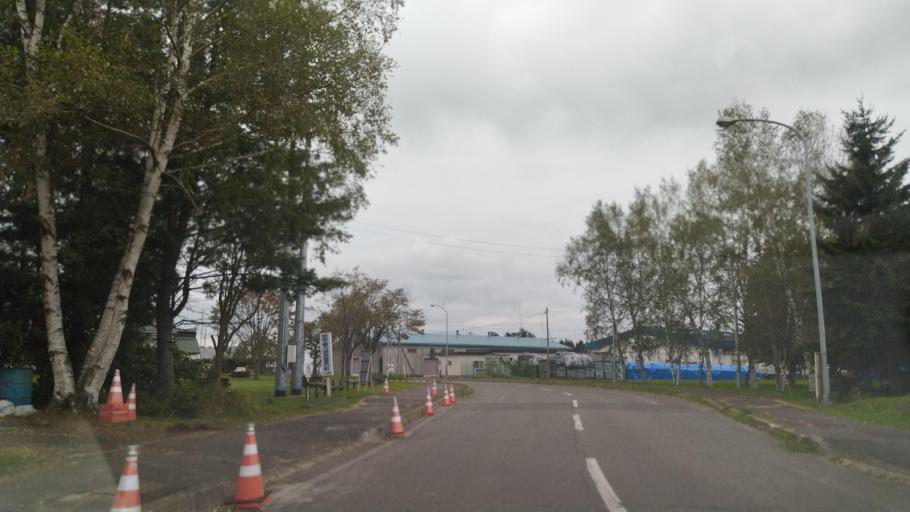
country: JP
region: Hokkaido
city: Otofuke
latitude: 43.2305
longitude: 143.2884
